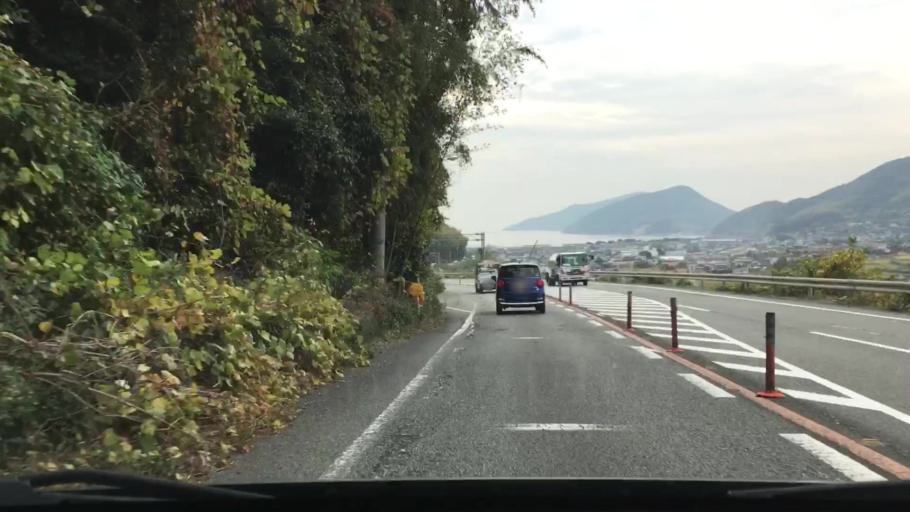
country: JP
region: Yamaguchi
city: Hofu
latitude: 34.0593
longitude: 131.6578
